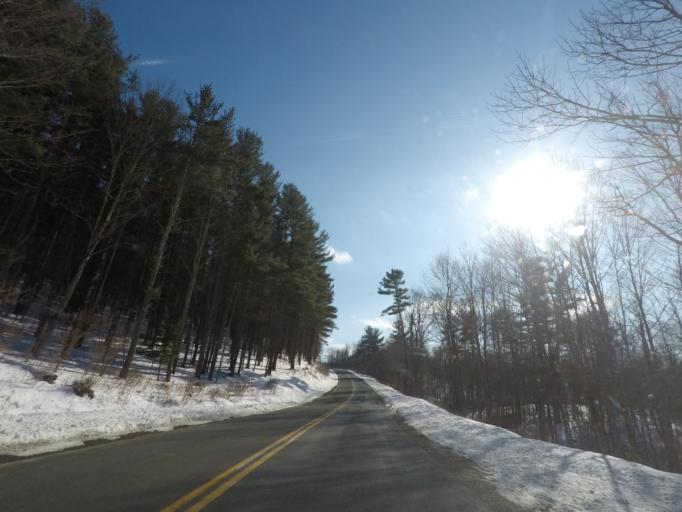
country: US
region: New York
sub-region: Rensselaer County
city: Hoosick Falls
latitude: 42.8895
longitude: -73.4955
